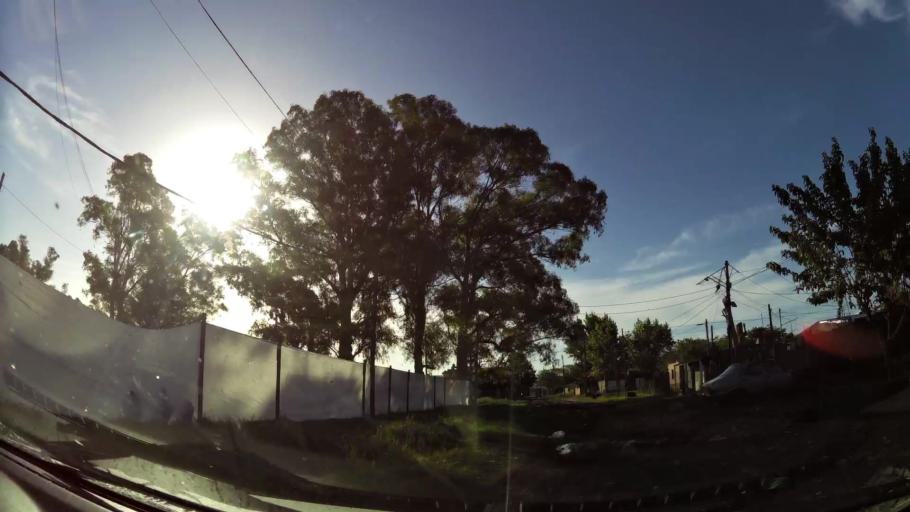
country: AR
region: Buenos Aires
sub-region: Partido de Quilmes
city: Quilmes
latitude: -34.8230
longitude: -58.2149
